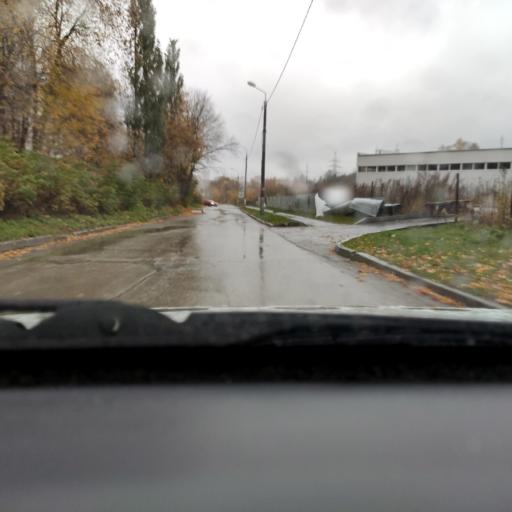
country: RU
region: Perm
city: Perm
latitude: 58.0105
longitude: 56.3134
